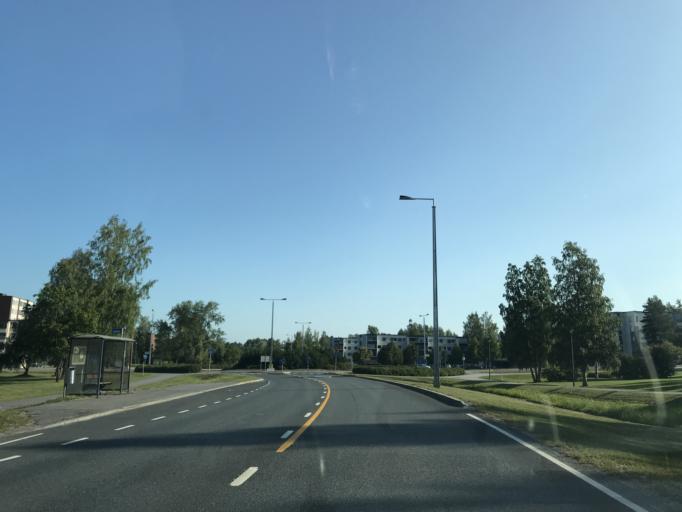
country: FI
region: Paijanne Tavastia
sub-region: Lahti
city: Orimattila
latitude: 60.8008
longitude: 25.7284
